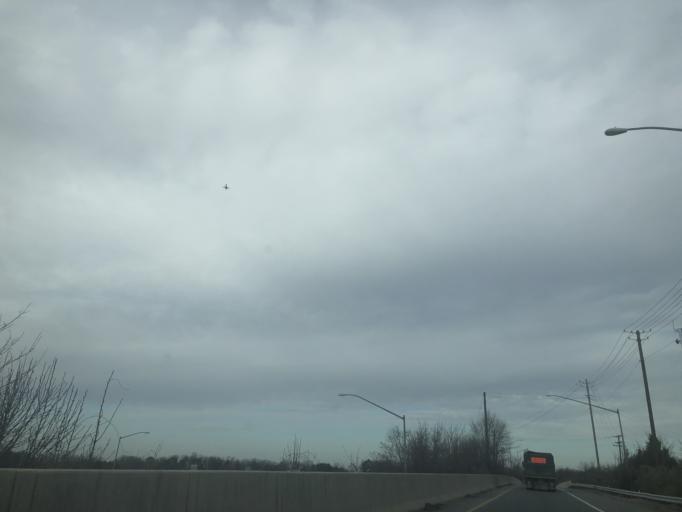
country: US
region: Maryland
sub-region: Prince George's County
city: Oxon Hill
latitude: 38.8011
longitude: -76.9970
